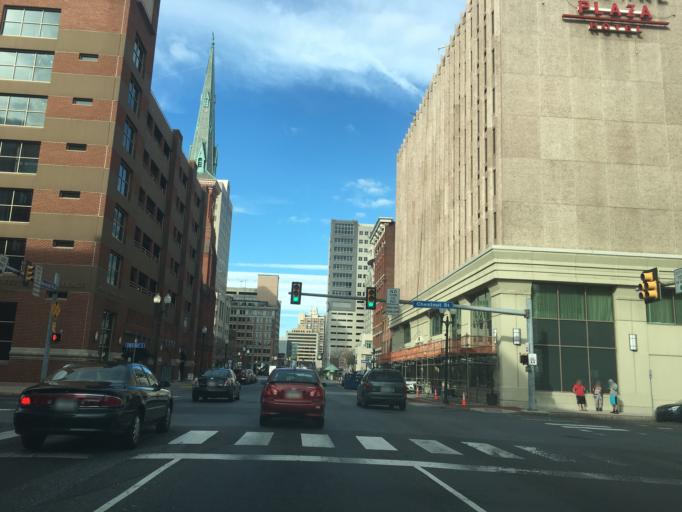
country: US
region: Pennsylvania
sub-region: Dauphin County
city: Harrisburg
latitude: 40.2588
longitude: -76.8801
